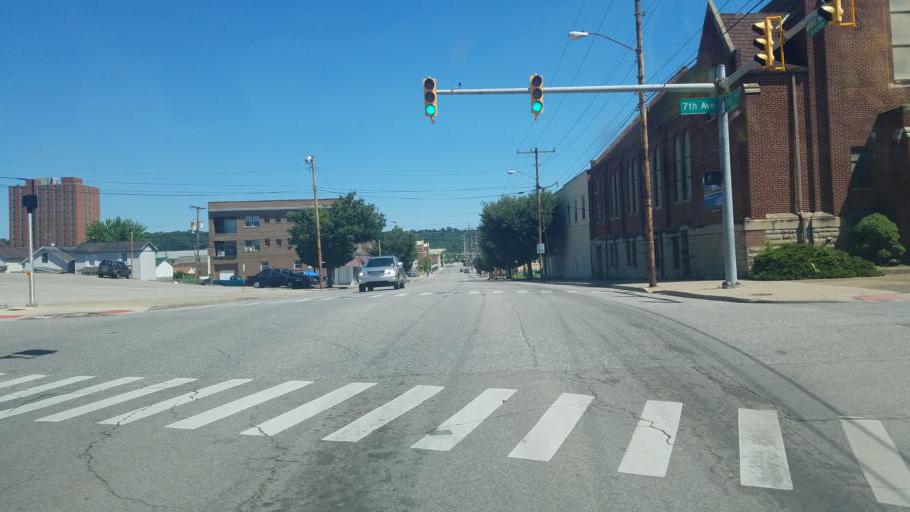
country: US
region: West Virginia
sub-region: Cabell County
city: Huntington
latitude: 38.4202
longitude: -82.4217
